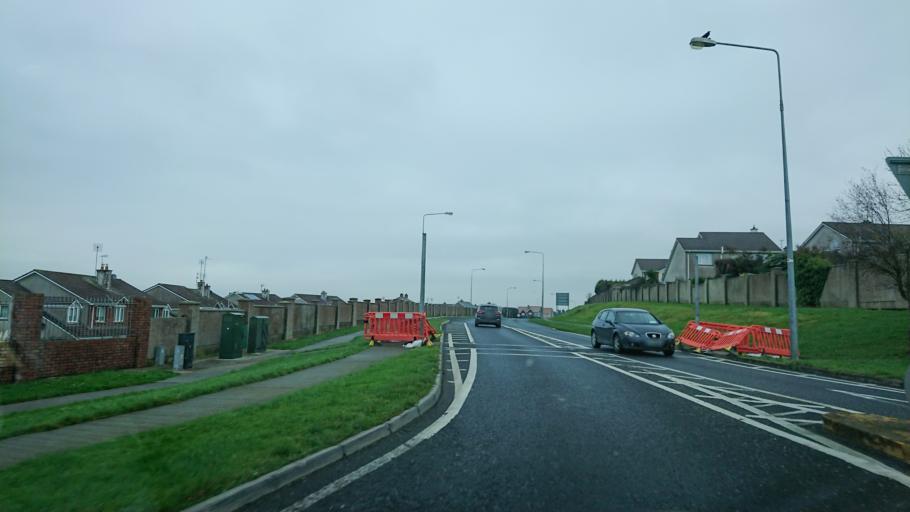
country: IE
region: Munster
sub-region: Waterford
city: Tra Mhor
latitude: 52.1660
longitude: -7.1639
